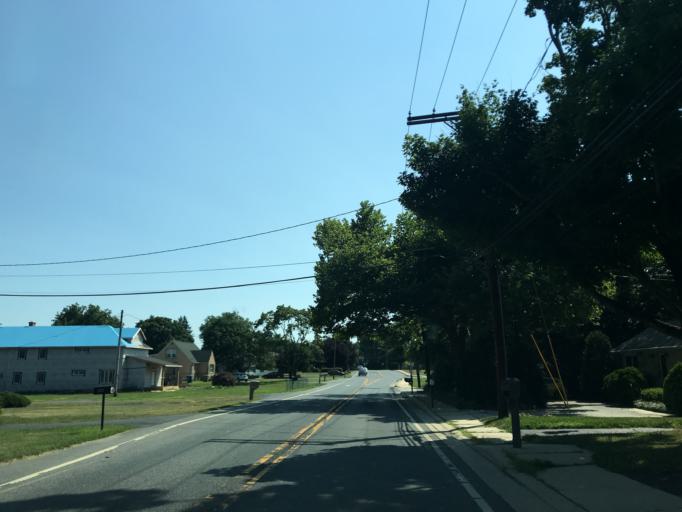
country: US
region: Delaware
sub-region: New Castle County
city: Bellefonte
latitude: 39.8311
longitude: -75.5223
